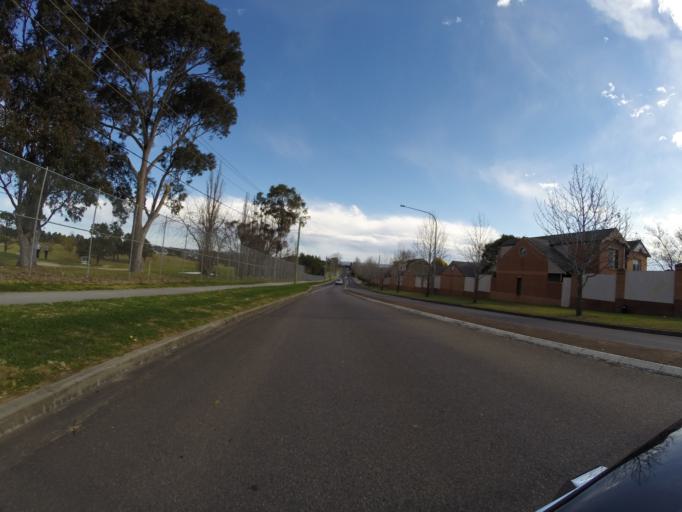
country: AU
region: New South Wales
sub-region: Camden
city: Narellan
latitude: -34.0436
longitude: 150.7260
